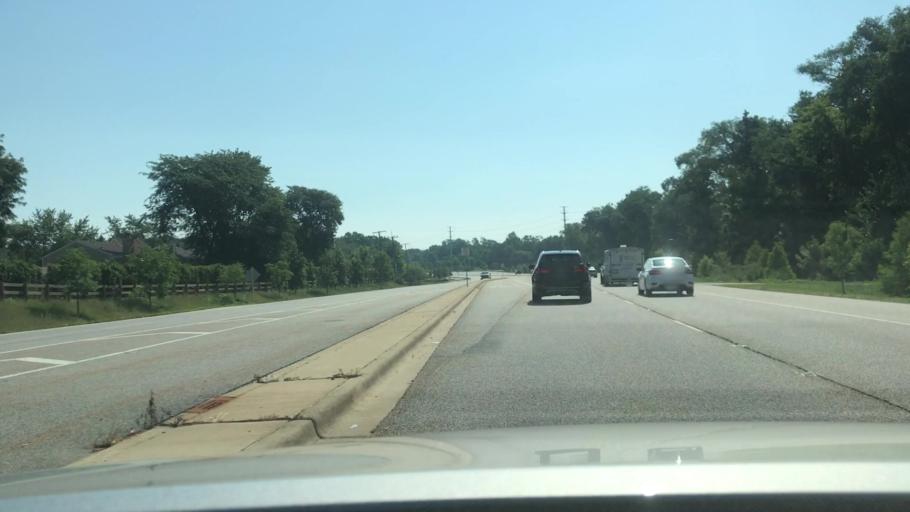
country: US
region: Illinois
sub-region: DuPage County
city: Warrenville
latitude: 41.8203
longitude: -88.1973
